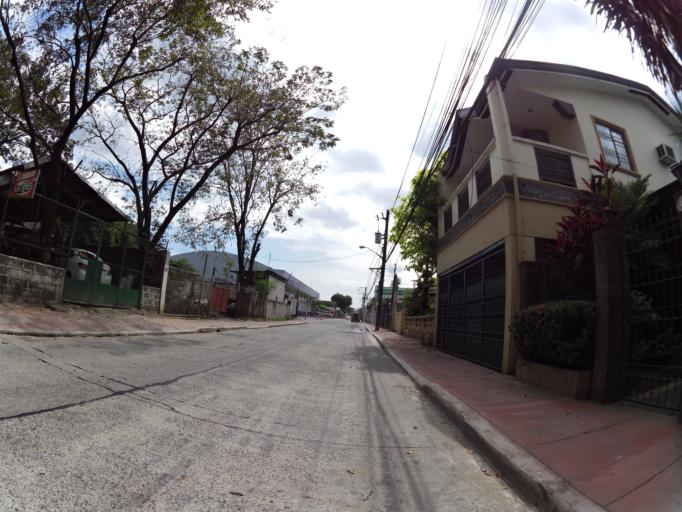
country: PH
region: Metro Manila
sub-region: Marikina
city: Calumpang
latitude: 14.6315
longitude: 121.1009
